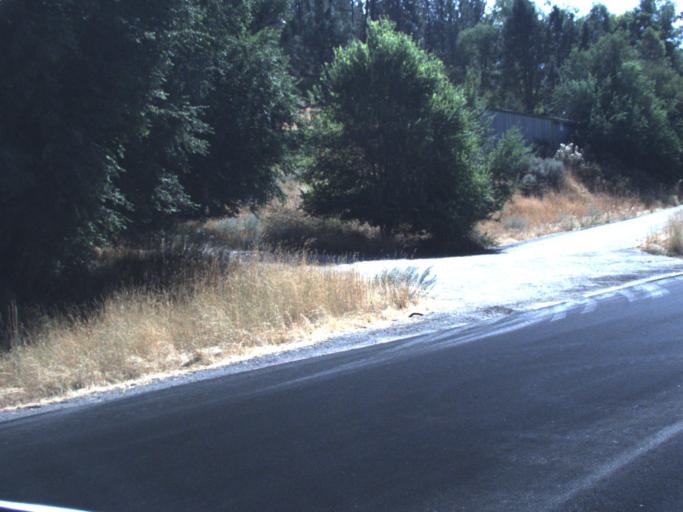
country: US
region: Washington
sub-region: Stevens County
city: Colville
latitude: 48.5237
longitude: -117.9029
